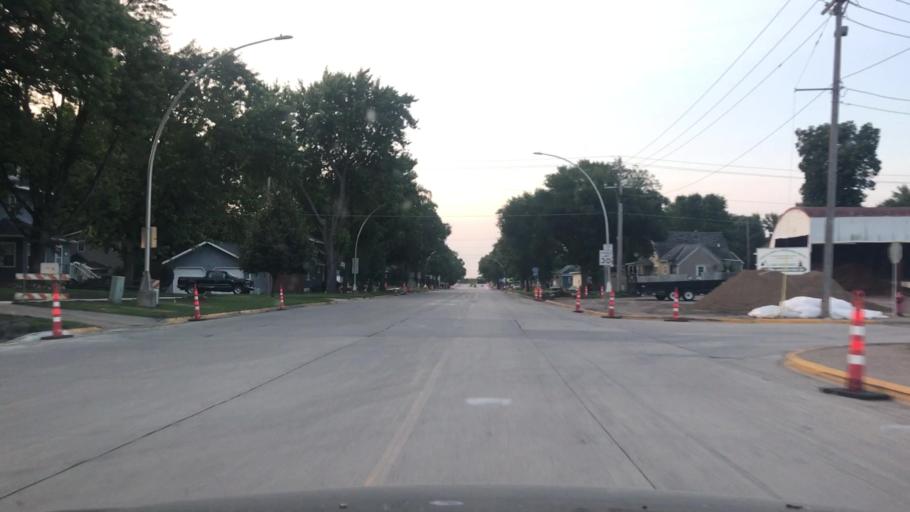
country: US
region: Minnesota
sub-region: Redwood County
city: Redwood Falls
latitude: 44.5331
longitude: -95.1195
